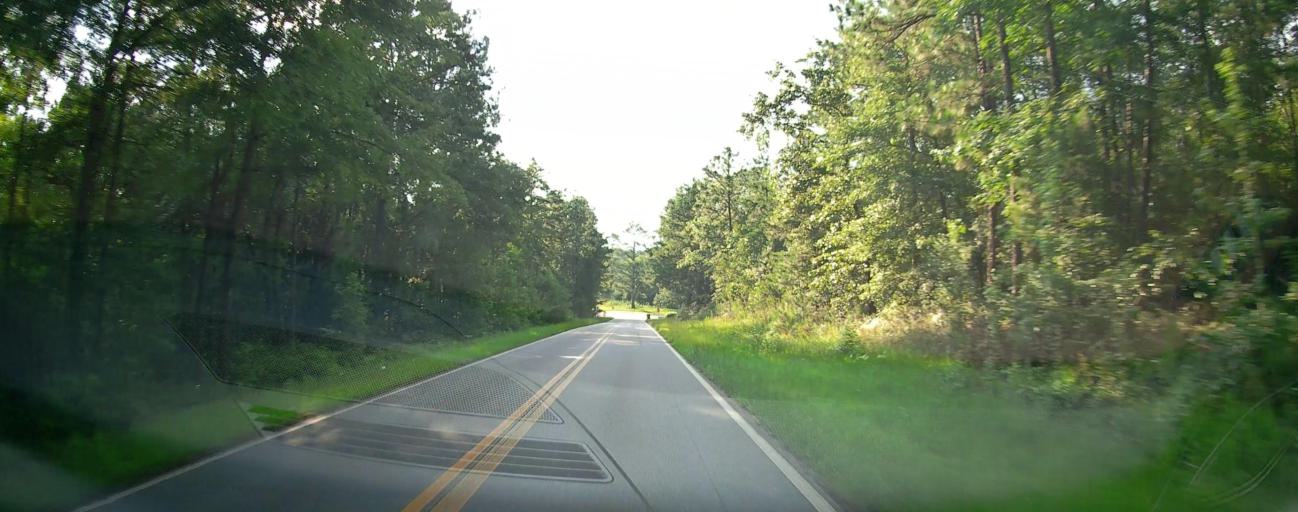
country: US
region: Georgia
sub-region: Bibb County
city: West Point
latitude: 32.7113
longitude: -83.8446
